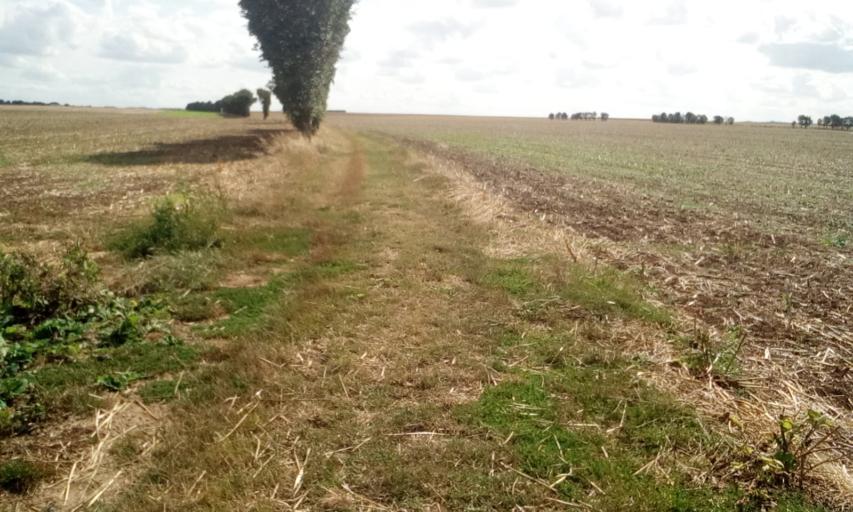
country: FR
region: Lower Normandy
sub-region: Departement du Calvados
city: Saint-Sylvain
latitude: 49.0877
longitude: -0.1964
